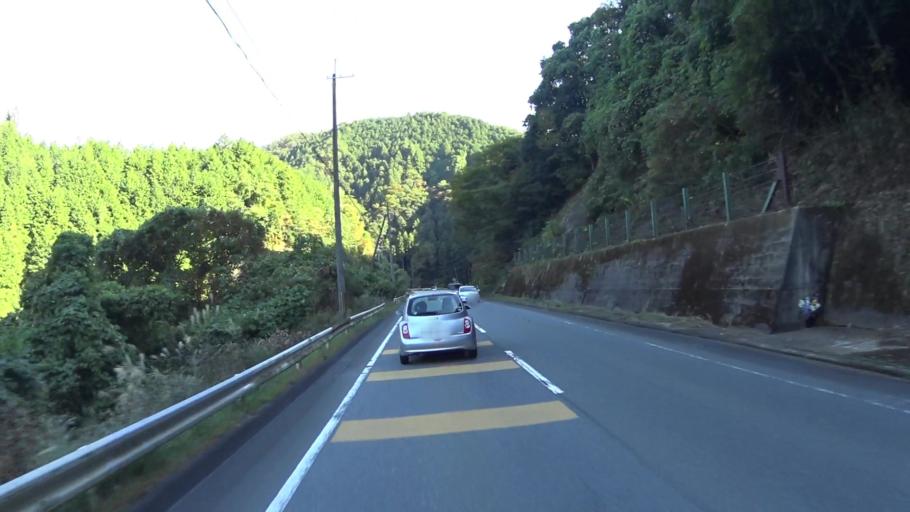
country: JP
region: Kyoto
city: Fukuchiyama
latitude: 35.3657
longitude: 135.1020
